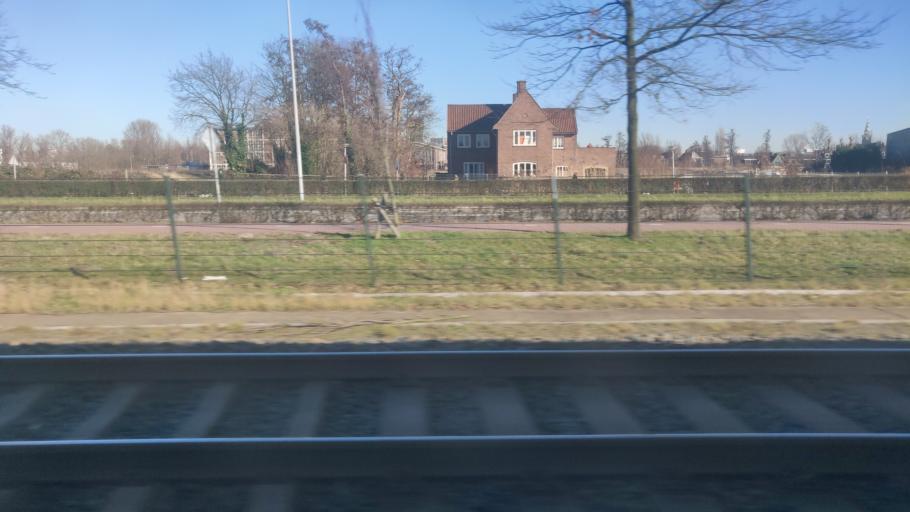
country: NL
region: North Holland
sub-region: Gemeente Zaanstad
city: Zaanstad
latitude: 52.4419
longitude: 4.8126
